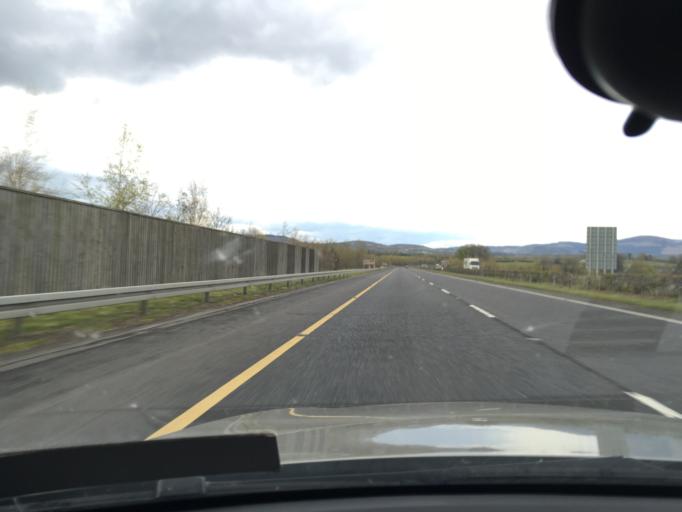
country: IE
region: Leinster
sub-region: Lu
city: Dundalk
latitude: 54.0268
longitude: -6.4356
